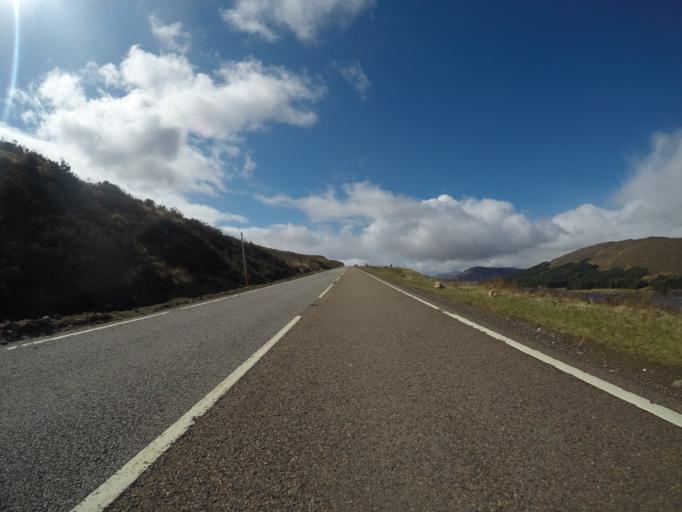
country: GB
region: Scotland
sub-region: Highland
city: Spean Bridge
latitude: 57.1175
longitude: -4.9804
